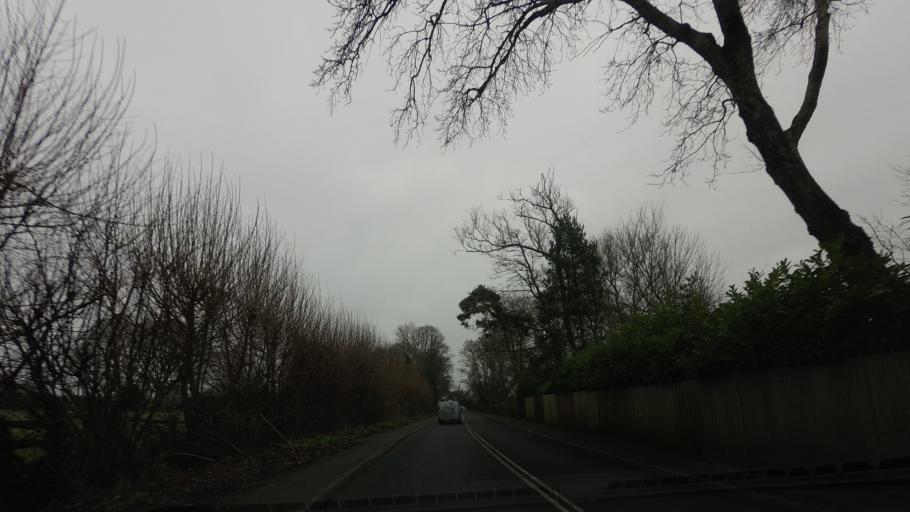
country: GB
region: England
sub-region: Kent
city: Hawkhurst
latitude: 51.0599
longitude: 0.5054
